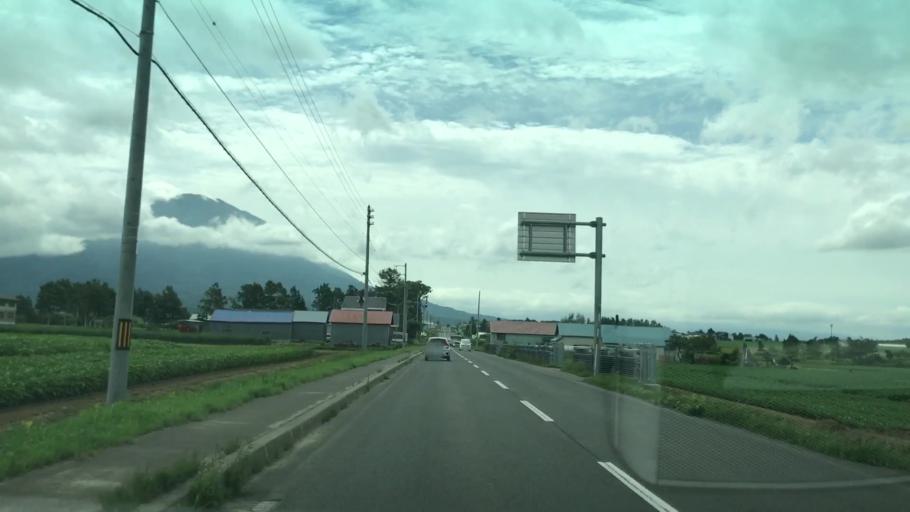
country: JP
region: Hokkaido
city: Niseko Town
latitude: 42.9308
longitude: 140.7758
